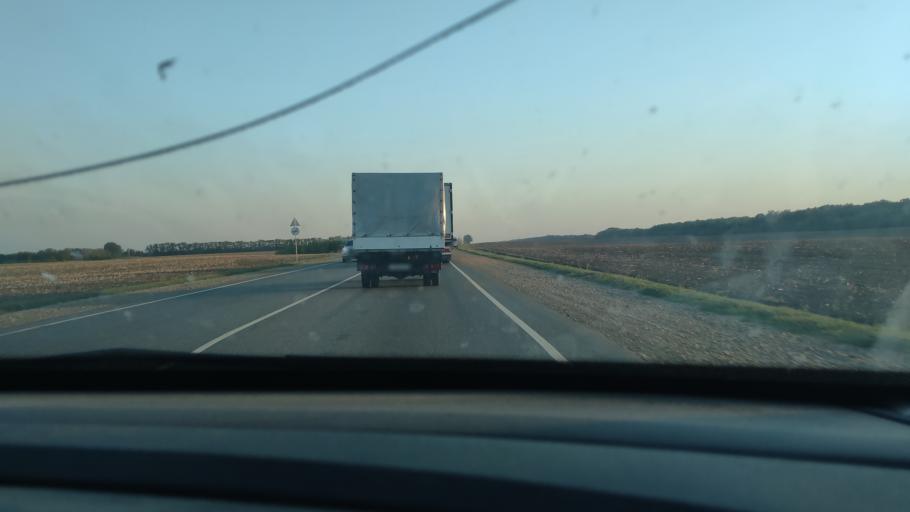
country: RU
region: Krasnodarskiy
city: Bryukhovetskaya
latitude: 45.7537
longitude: 38.9876
